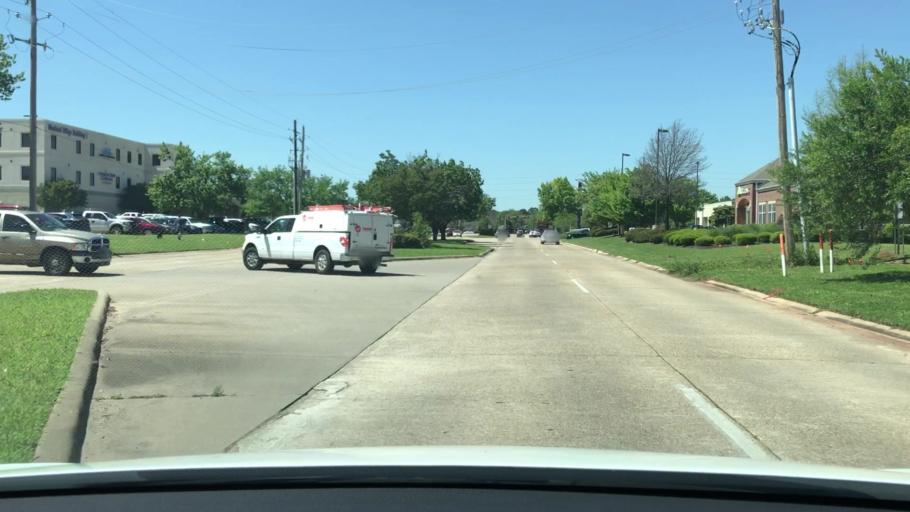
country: US
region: Louisiana
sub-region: Bossier Parish
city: Bossier City
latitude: 32.4261
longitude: -93.7153
